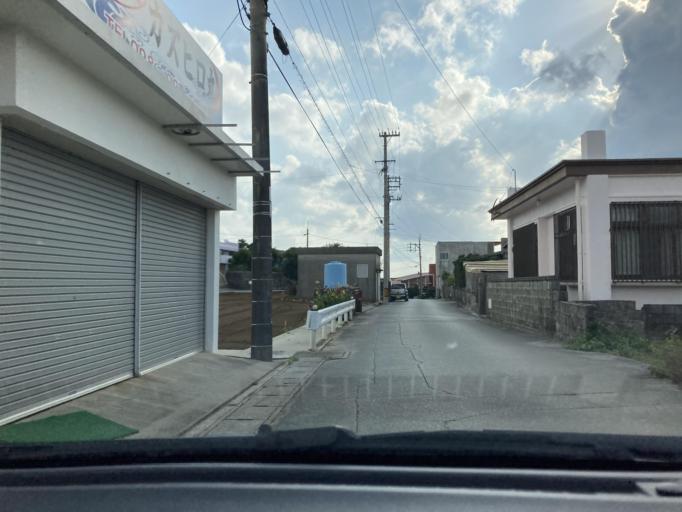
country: JP
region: Okinawa
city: Itoman
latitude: 26.0908
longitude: 127.6619
